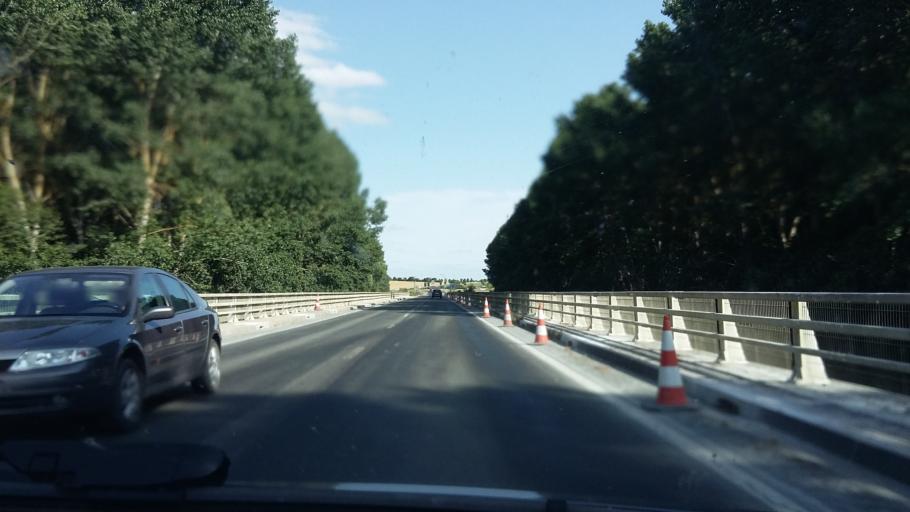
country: FR
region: Poitou-Charentes
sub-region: Departement de la Charente-Maritime
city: Saint-Jean-d'Angely
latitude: 45.9412
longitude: -0.4874
